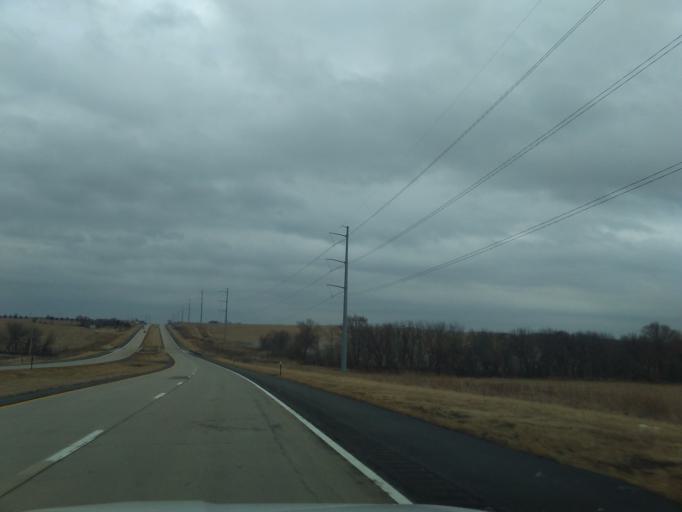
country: US
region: Nebraska
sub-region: Otoe County
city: Syracuse
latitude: 40.6682
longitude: -96.1522
